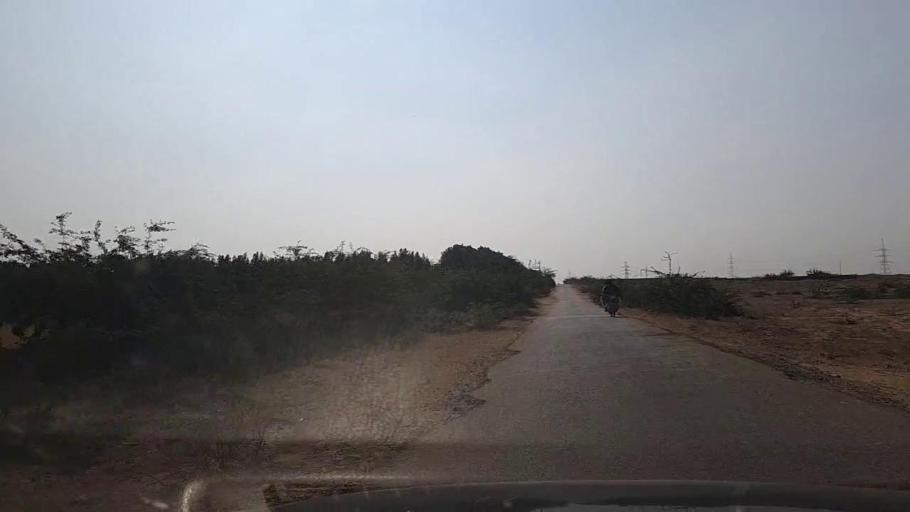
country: PK
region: Sindh
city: Gharo
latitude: 24.7715
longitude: 67.5574
